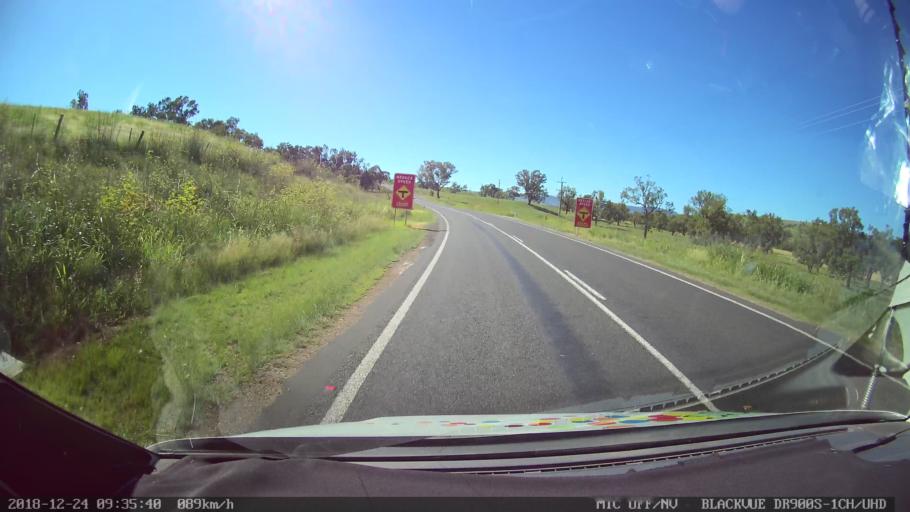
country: AU
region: New South Wales
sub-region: Liverpool Plains
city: Quirindi
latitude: -31.6322
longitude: 150.7188
